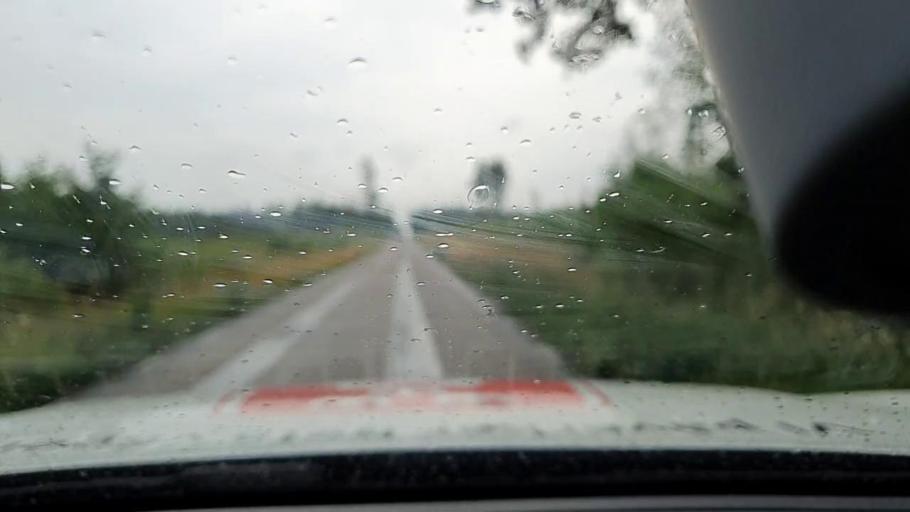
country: SE
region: Vaestra Goetaland
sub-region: Skovde Kommun
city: Skoevde
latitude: 58.4416
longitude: 13.7633
